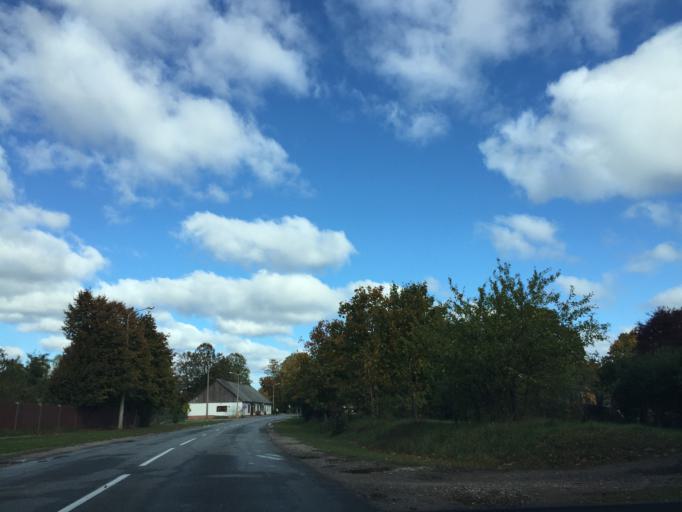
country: LV
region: Tukuma Rajons
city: Engure
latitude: 57.1572
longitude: 23.2290
